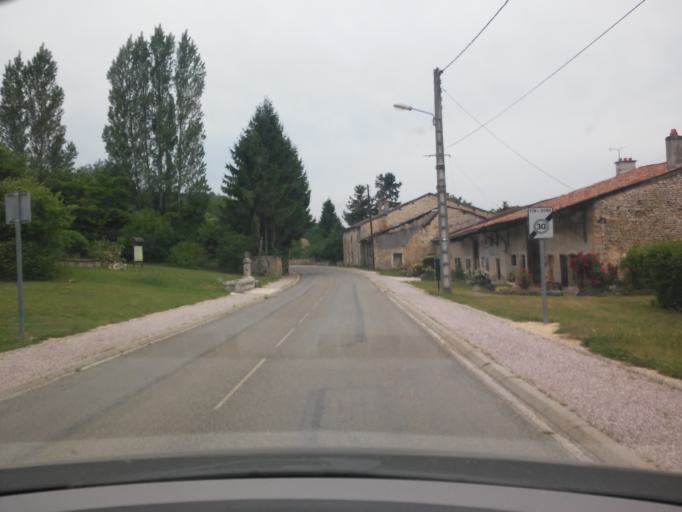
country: FR
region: Lorraine
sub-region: Departement de la Meuse
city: Vignot
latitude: 48.8041
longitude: 5.6270
